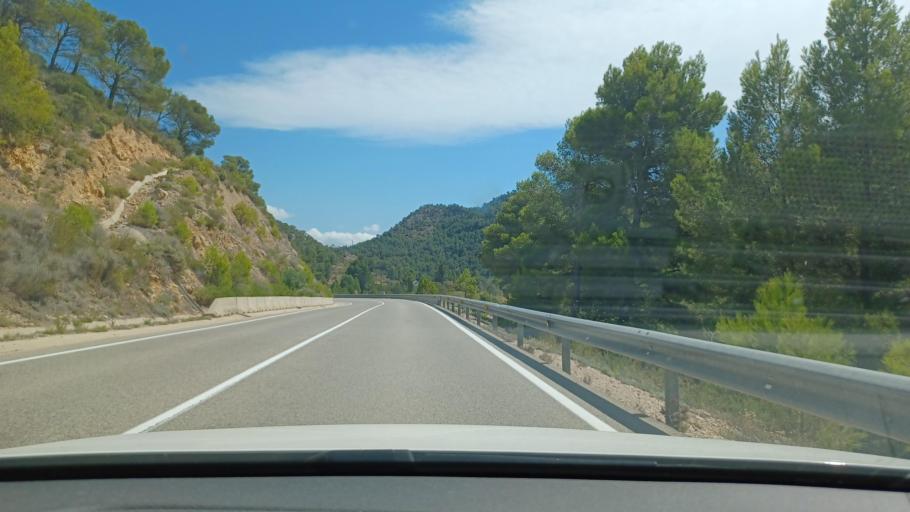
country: ES
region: Catalonia
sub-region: Provincia de Tarragona
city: Bot
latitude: 40.9751
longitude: 0.4237
